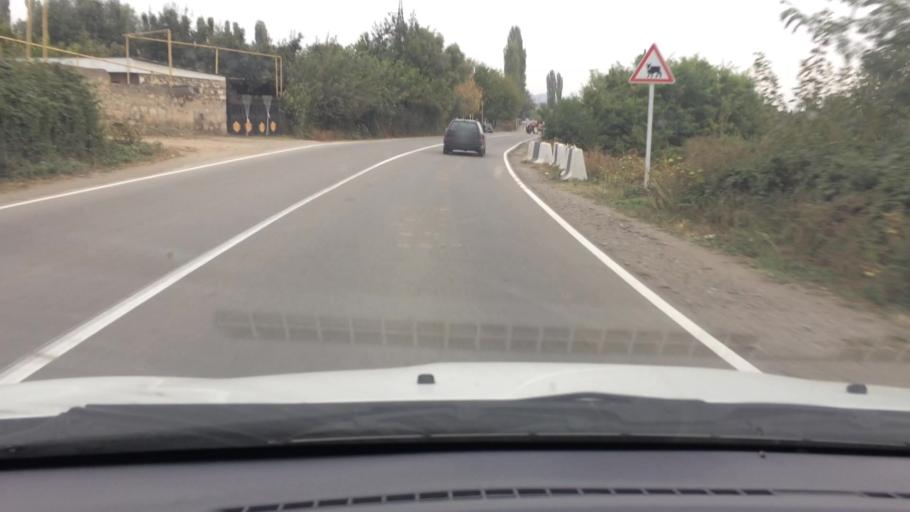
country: GE
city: Naghvarevi
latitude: 41.3251
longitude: 44.8002
